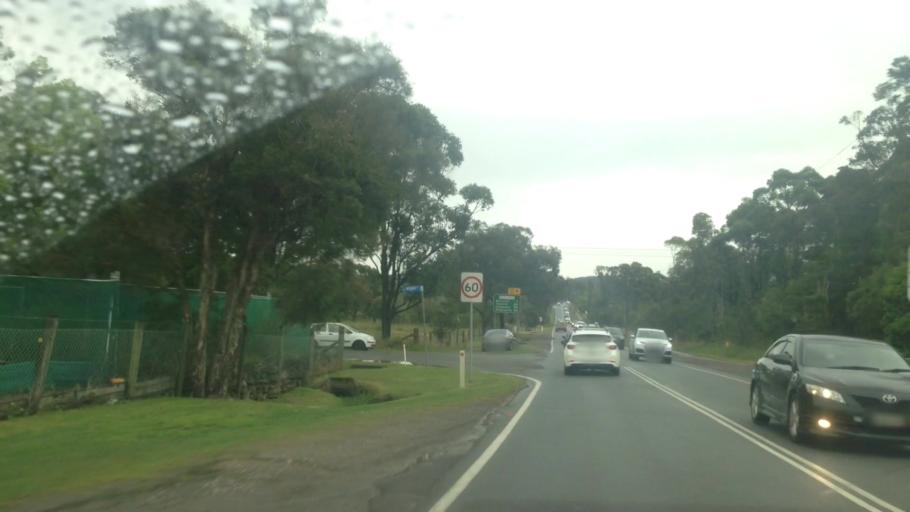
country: AU
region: New South Wales
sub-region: Wyong Shire
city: Charmhaven
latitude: -33.1747
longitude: 151.4800
